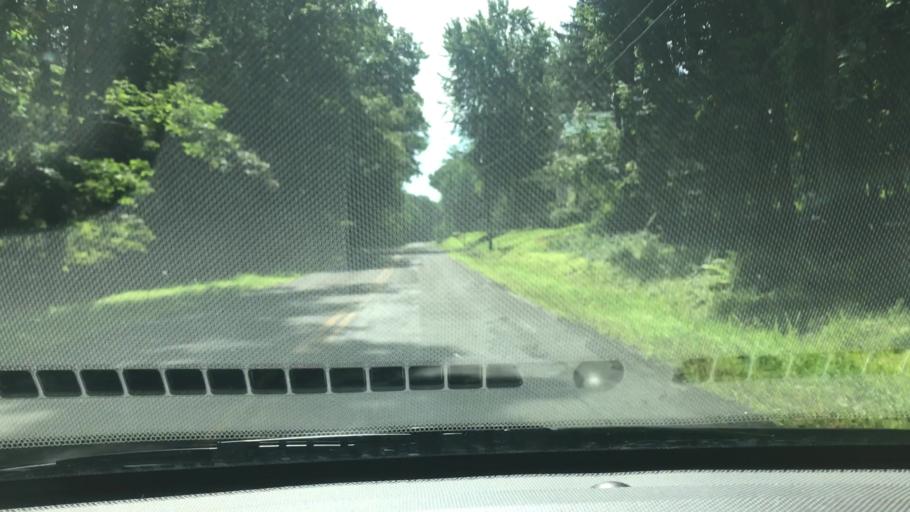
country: US
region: New York
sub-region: Ulster County
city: Shokan
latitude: 41.9574
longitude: -74.2663
